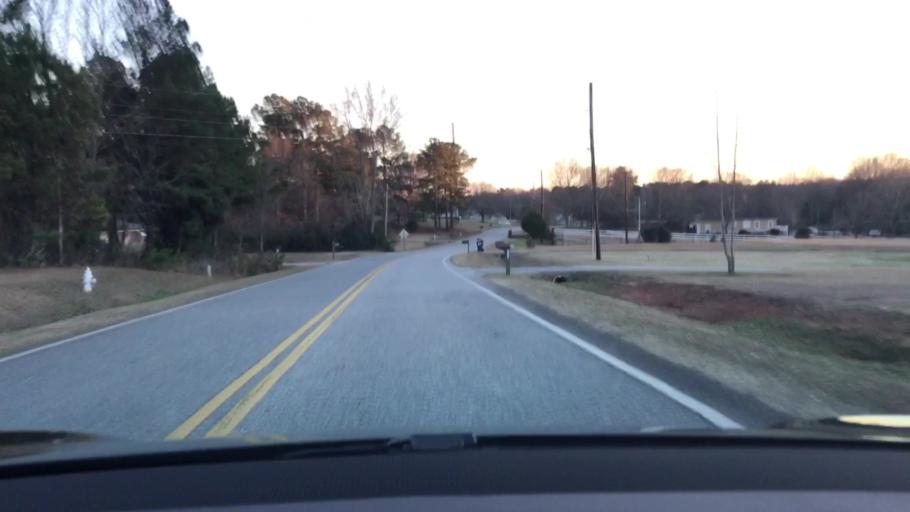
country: US
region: Georgia
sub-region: Gwinnett County
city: Grayson
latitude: 33.8859
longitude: -83.9153
